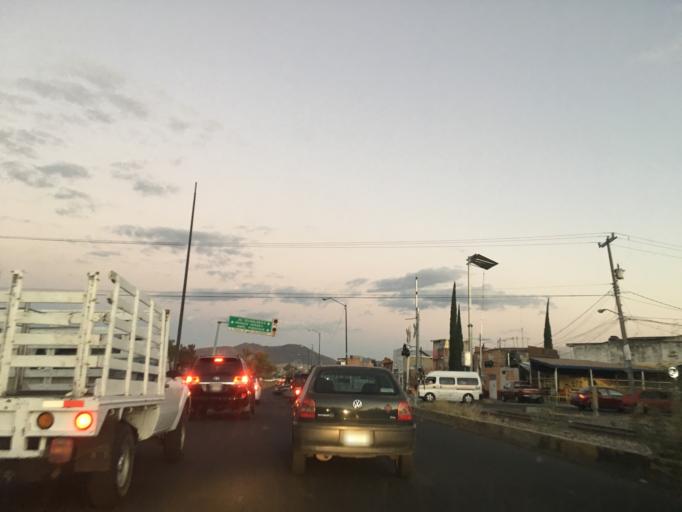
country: MX
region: Michoacan
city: Morelia
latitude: 19.7142
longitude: -101.2020
